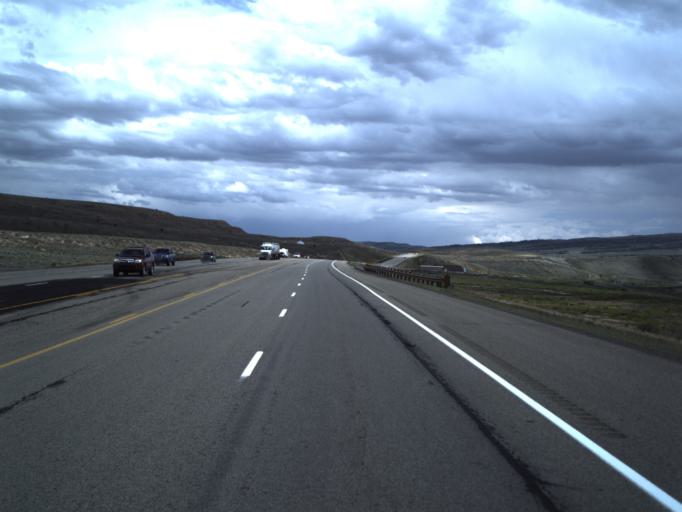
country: US
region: Utah
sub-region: Carbon County
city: Helper
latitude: 39.8581
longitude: -111.0225
